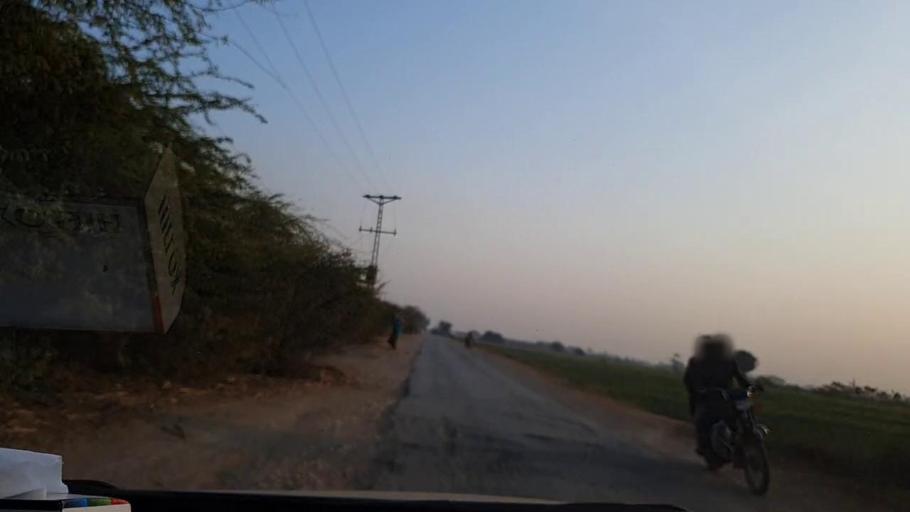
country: PK
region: Sindh
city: Tando Ghulam Ali
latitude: 25.1792
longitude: 68.9490
